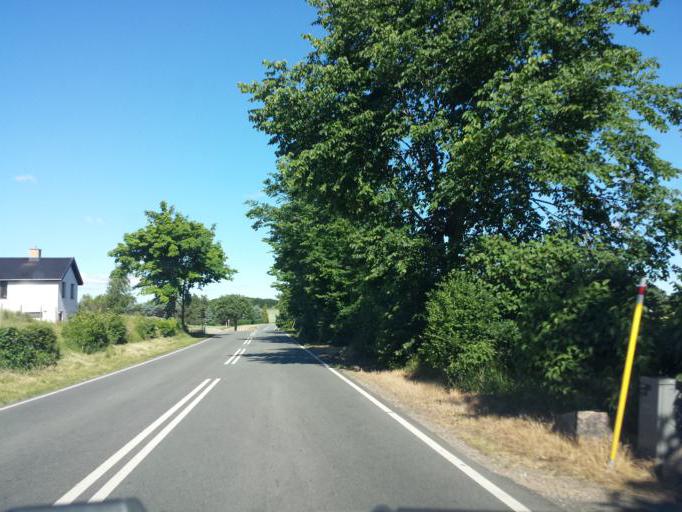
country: DK
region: Capital Region
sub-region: Egedal Kommune
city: Ganlose
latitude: 55.7802
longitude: 12.2863
